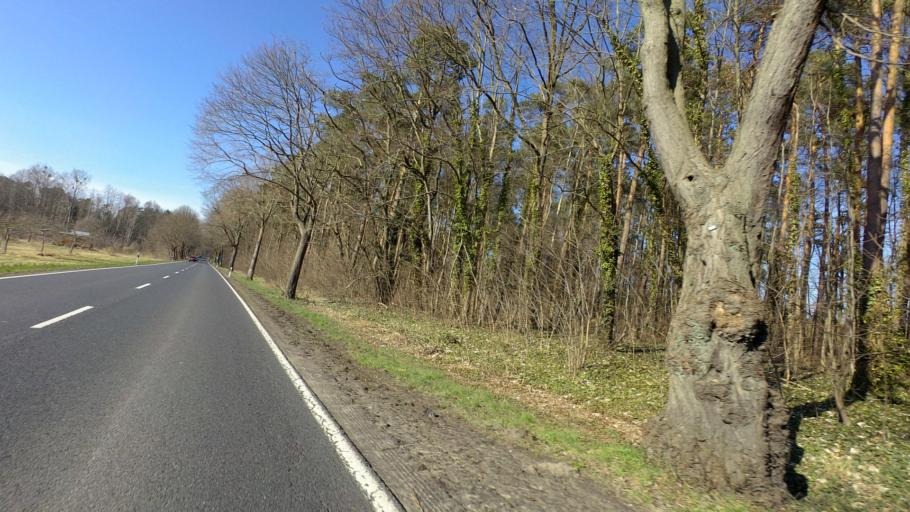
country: DE
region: Brandenburg
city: Chorin
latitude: 52.8963
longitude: 13.8919
